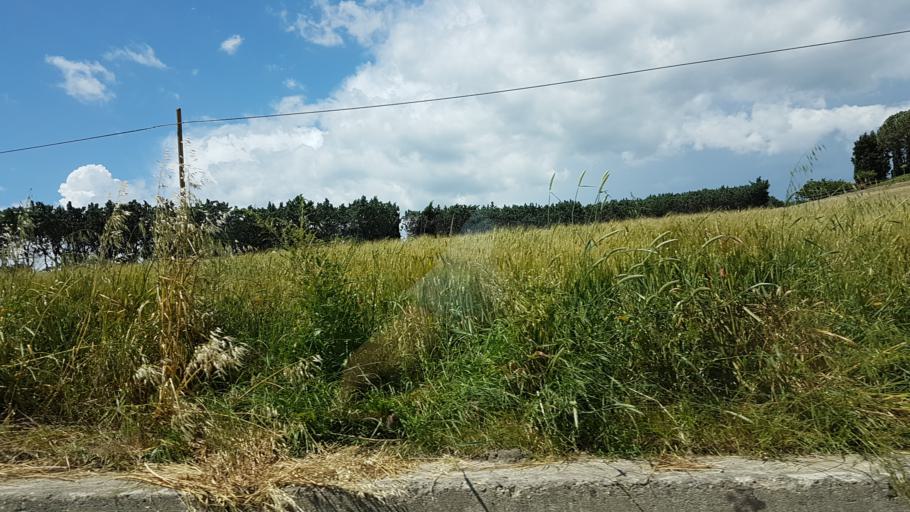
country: IT
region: Tuscany
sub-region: Province of Pisa
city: Orciano Pisano
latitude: 43.4511
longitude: 10.5144
